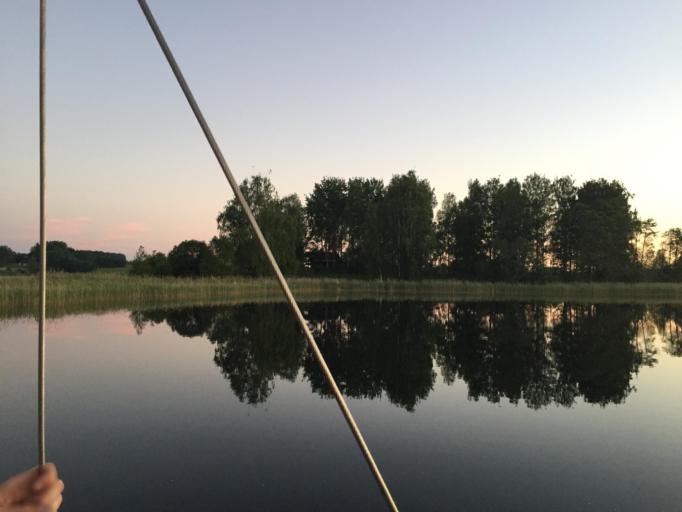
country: LV
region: Rezekne
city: Rezekne
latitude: 56.3693
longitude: 27.4157
